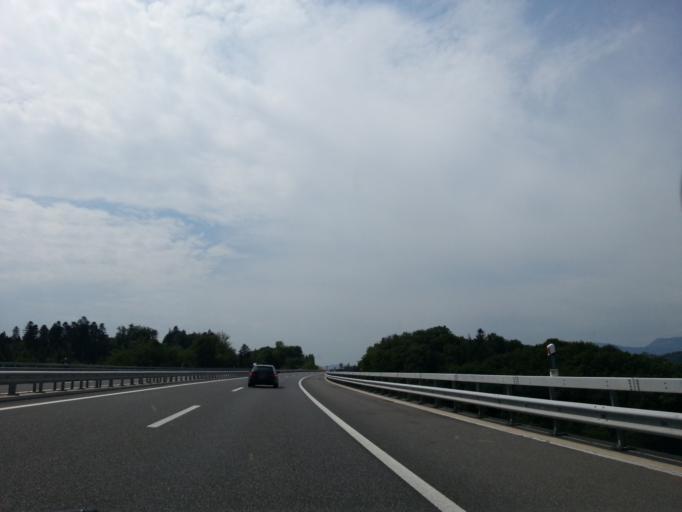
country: CH
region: Vaud
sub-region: Jura-Nord vaudois District
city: Yvonand
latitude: 46.7770
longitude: 6.7257
